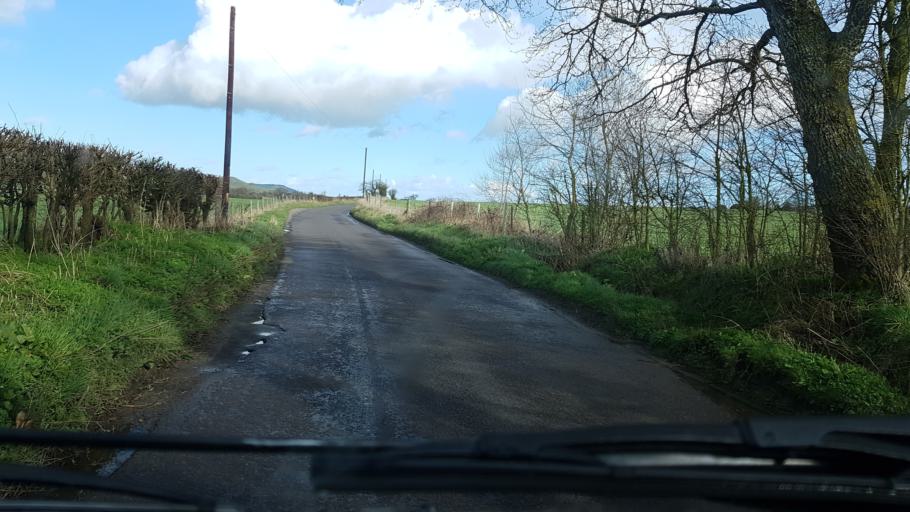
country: GB
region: England
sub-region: Wiltshire
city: Woodborough
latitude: 51.3326
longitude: -1.8613
